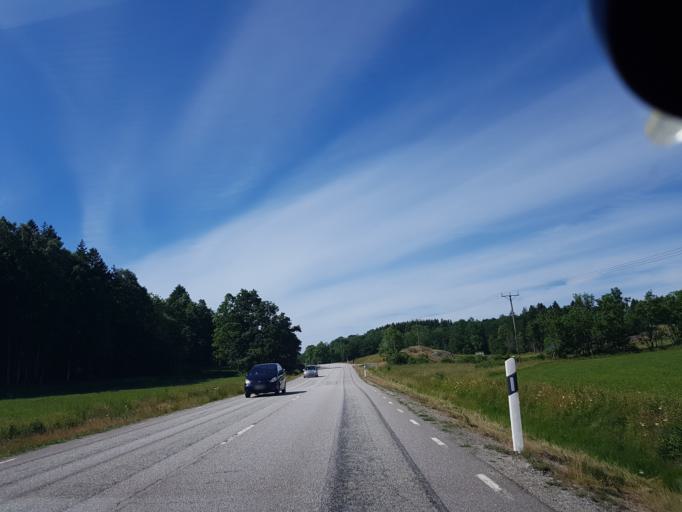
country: SE
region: Vaestra Goetaland
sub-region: Lysekils Kommun
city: Lysekil
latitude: 58.1658
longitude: 11.4808
